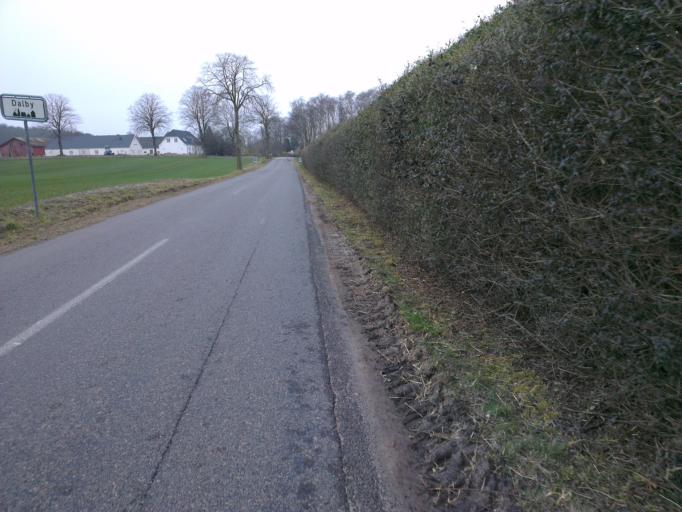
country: DK
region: Capital Region
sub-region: Frederikssund Kommune
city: Skibby
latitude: 55.7930
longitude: 11.9628
